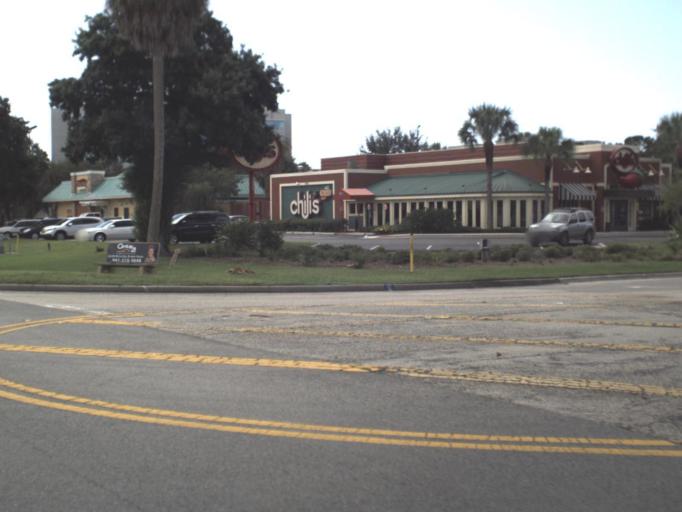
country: US
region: Florida
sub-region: Charlotte County
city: Port Charlotte
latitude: 27.0116
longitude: -82.1435
